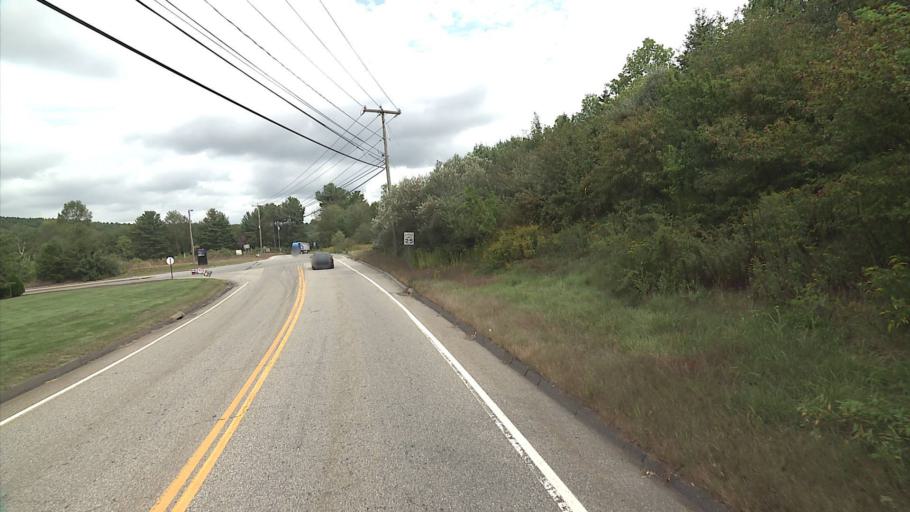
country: US
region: Connecticut
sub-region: Tolland County
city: Stafford Springs
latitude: 41.9181
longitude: -72.2603
